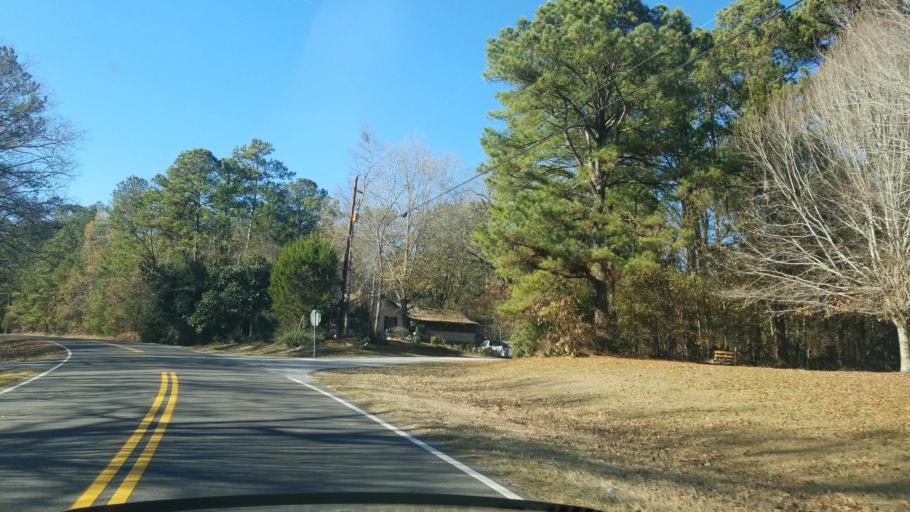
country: US
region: Georgia
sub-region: Harris County
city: Hamilton
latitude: 32.6682
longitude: -84.8772
